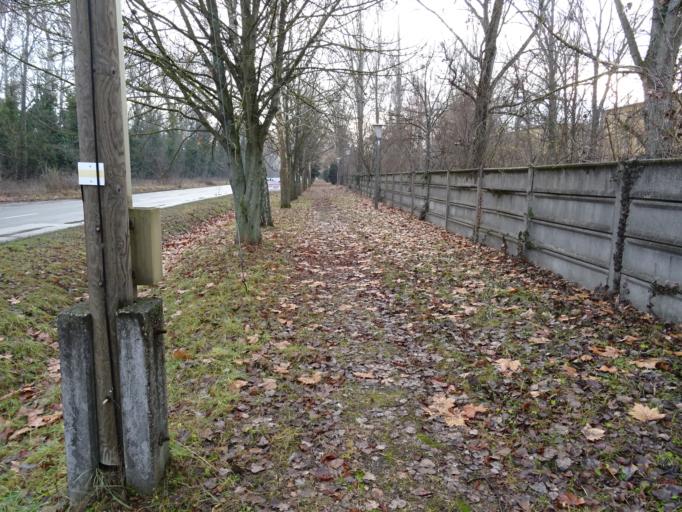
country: HU
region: Bacs-Kiskun
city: Szabadszallas
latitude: 46.8932
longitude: 19.2192
